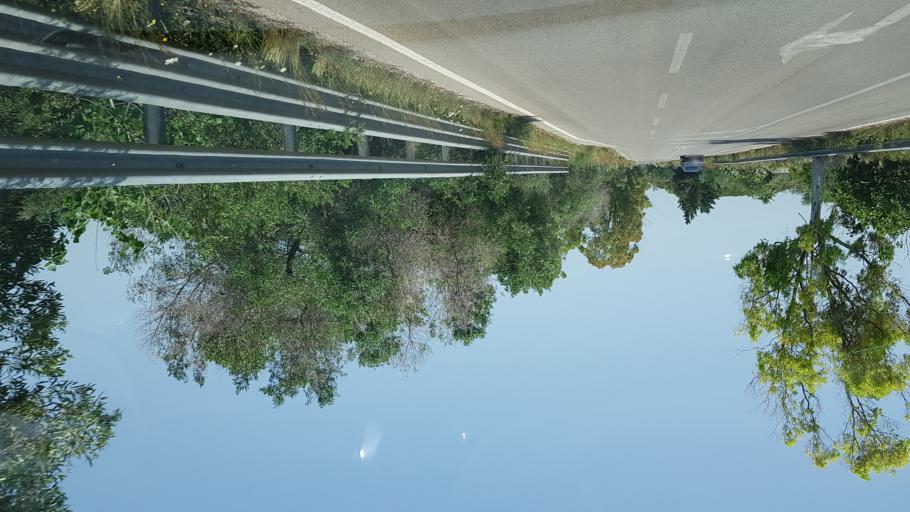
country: IT
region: Apulia
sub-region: Provincia di Lecce
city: Porto Cesareo
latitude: 40.2578
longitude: 17.9252
